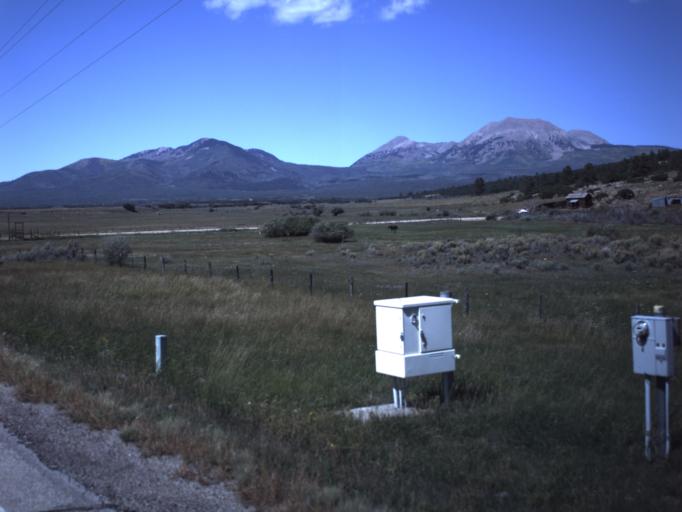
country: US
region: Utah
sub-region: Grand County
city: Moab
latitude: 38.3265
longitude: -109.1236
